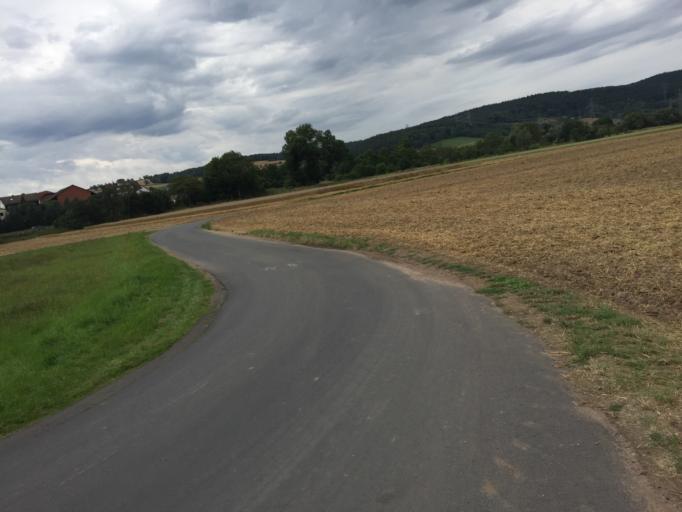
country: DE
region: Hesse
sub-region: Regierungsbezirk Kassel
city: Bad Hersfeld
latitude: 50.9031
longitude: 9.7515
